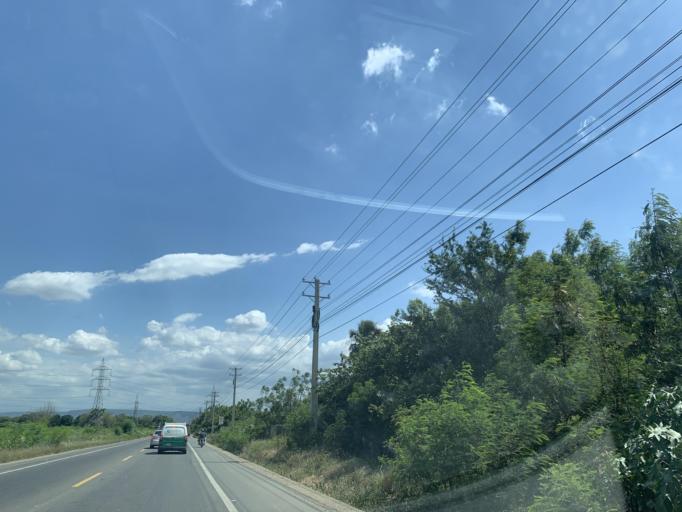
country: DO
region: Santiago
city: Villa Bisono
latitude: 19.5636
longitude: -70.8579
